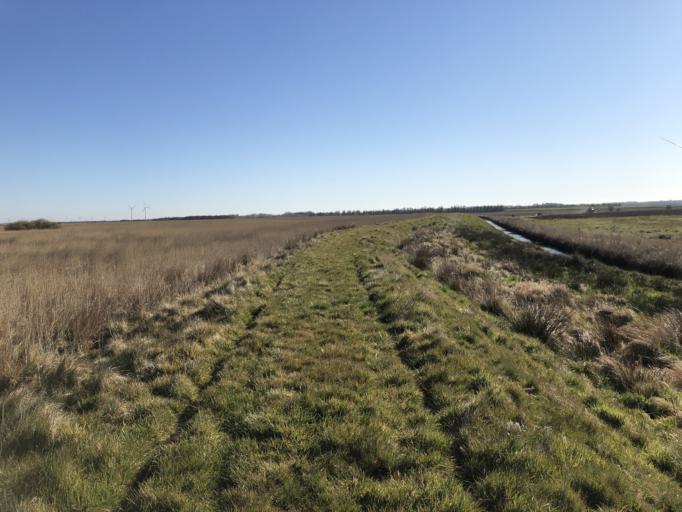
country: DK
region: Central Jutland
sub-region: Holstebro Kommune
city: Ulfborg
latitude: 56.2997
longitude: 8.2821
